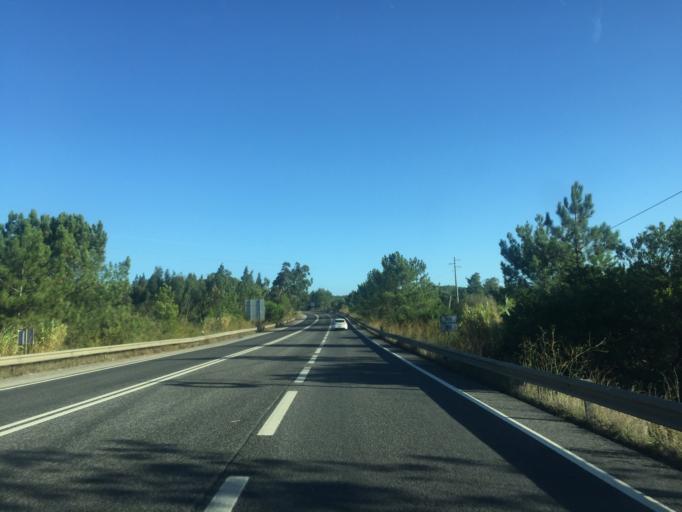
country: PT
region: Lisbon
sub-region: Azambuja
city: Alcoentre
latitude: 39.2463
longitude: -8.9539
